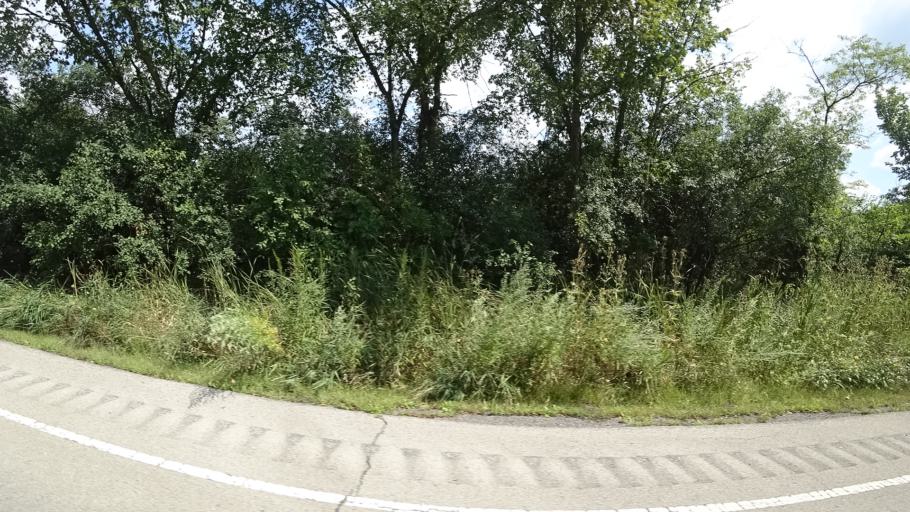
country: US
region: Illinois
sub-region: Cook County
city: Oak Forest
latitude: 41.6179
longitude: -87.7858
